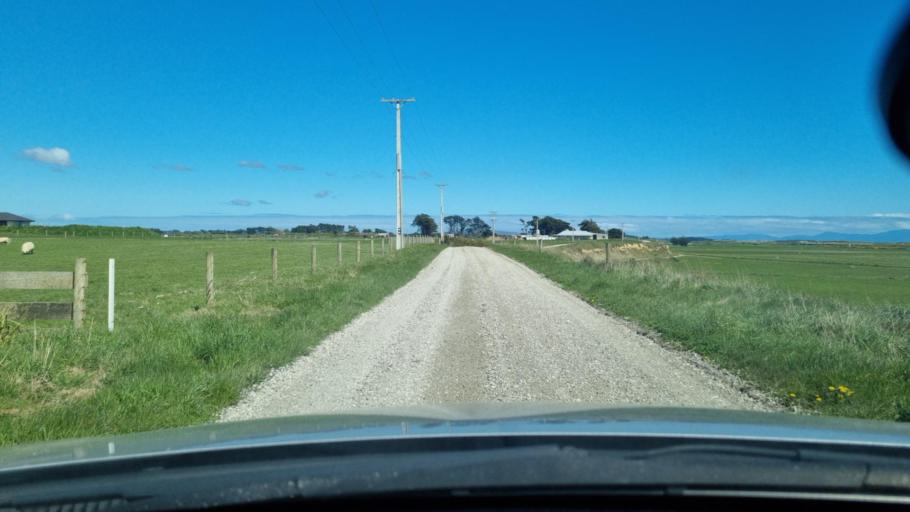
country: NZ
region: Southland
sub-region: Invercargill City
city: Invercargill
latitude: -46.3960
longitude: 168.2577
